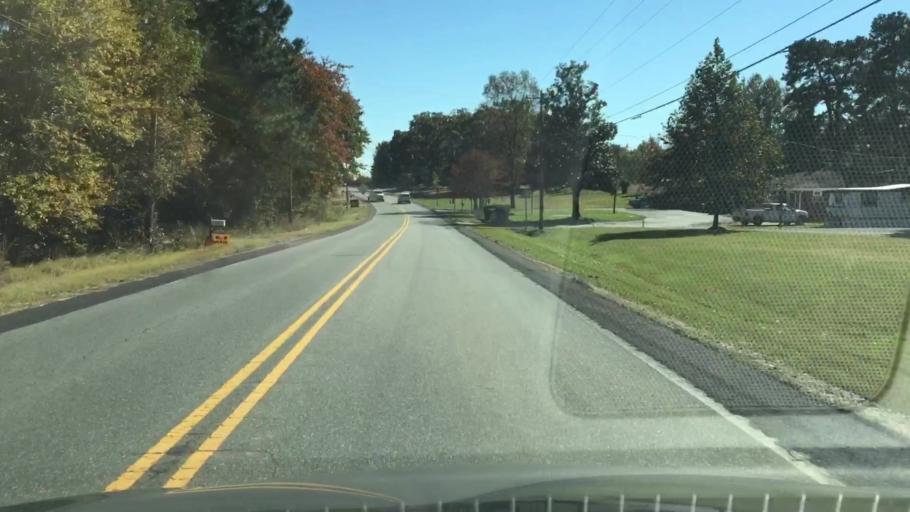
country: US
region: North Carolina
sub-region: Rockingham County
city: Reidsville
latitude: 36.2984
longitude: -79.6631
